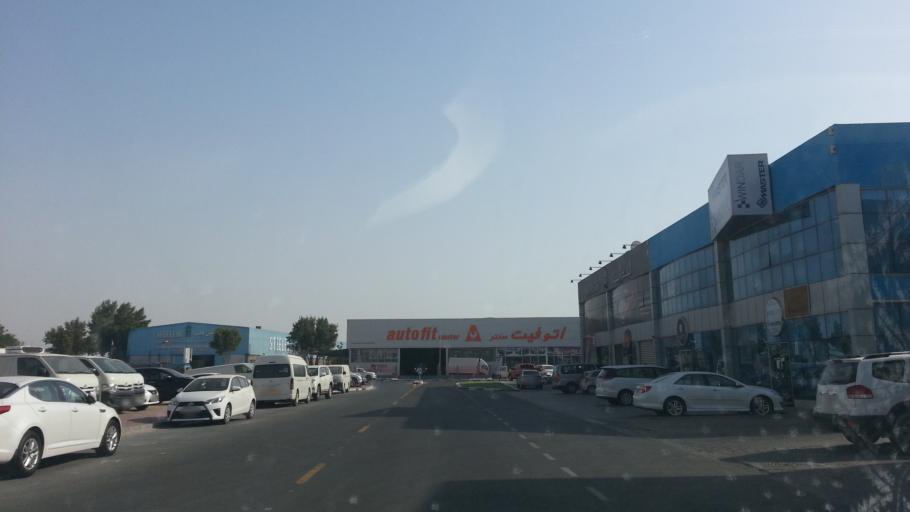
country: AE
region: Dubai
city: Dubai
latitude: 25.1505
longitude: 55.2274
